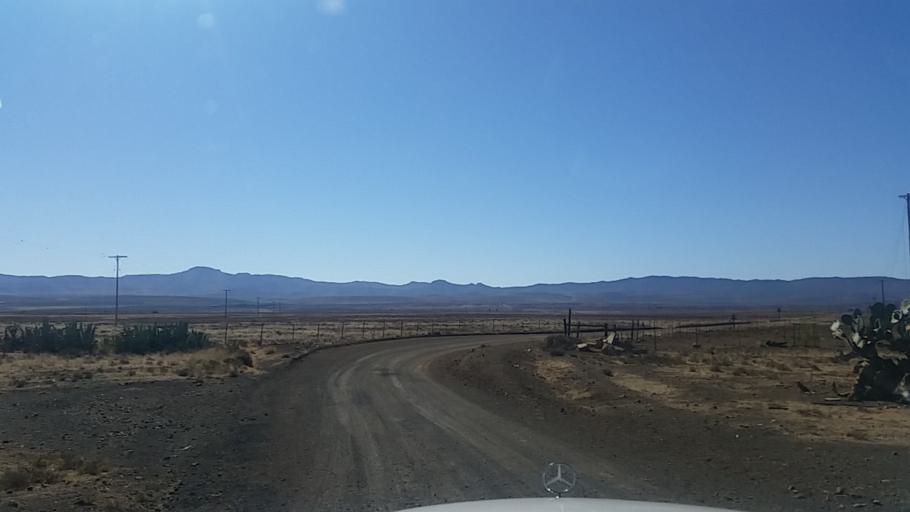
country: ZA
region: Eastern Cape
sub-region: Cacadu District Municipality
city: Graaff-Reinet
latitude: -31.9067
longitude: 24.7582
